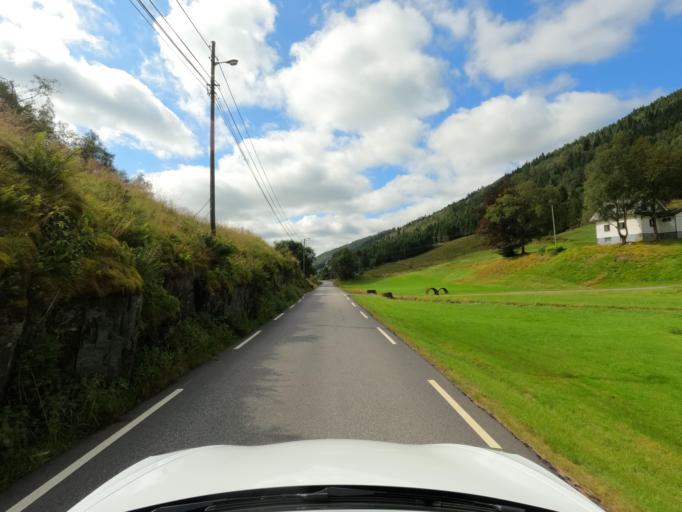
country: NO
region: Hordaland
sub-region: Os
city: Syfteland
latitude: 60.2910
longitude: 5.4784
